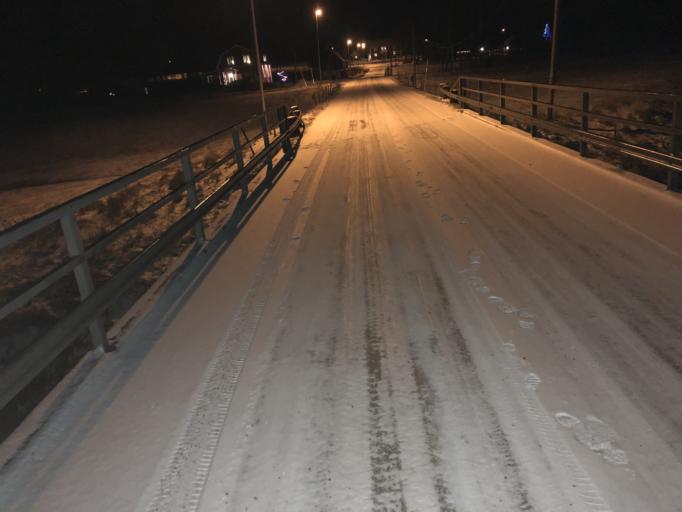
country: SE
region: Kronoberg
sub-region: Ljungby Kommun
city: Ljungby
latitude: 56.7098
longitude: 13.9452
